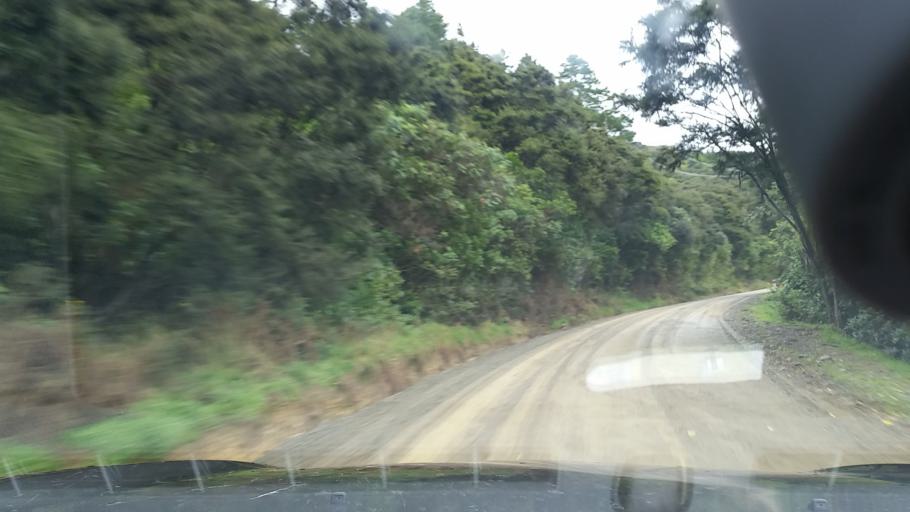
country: NZ
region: Marlborough
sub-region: Marlborough District
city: Picton
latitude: -41.3603
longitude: 174.0697
